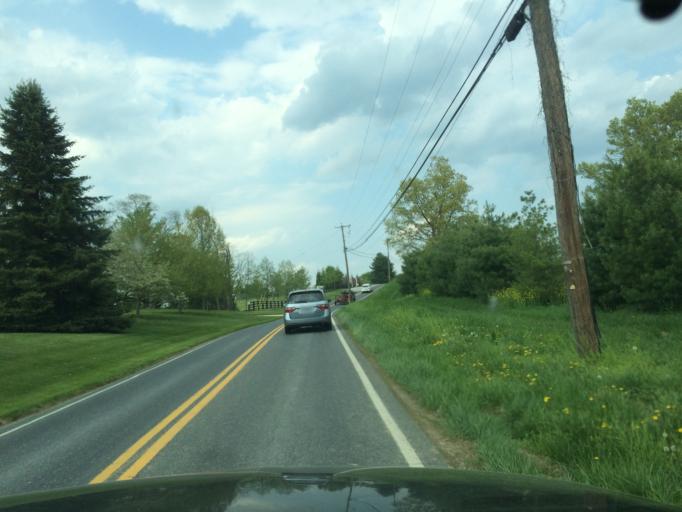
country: US
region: Maryland
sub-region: Carroll County
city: Sykesville
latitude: 39.3022
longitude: -76.9870
